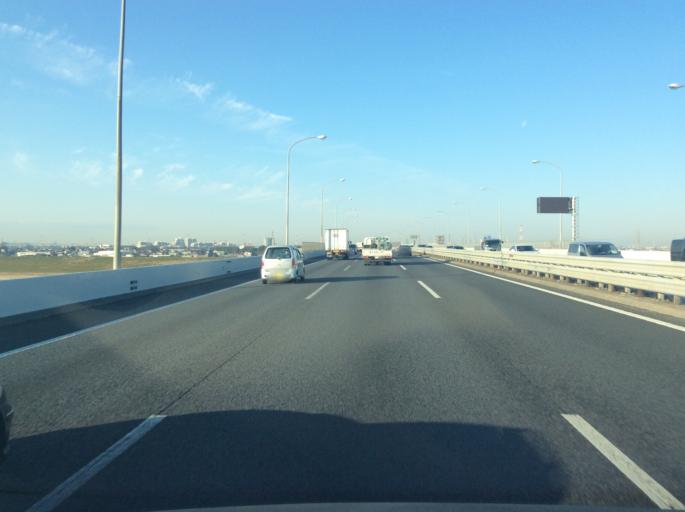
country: JP
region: Chiba
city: Nagareyama
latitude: 35.8760
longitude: 139.8956
